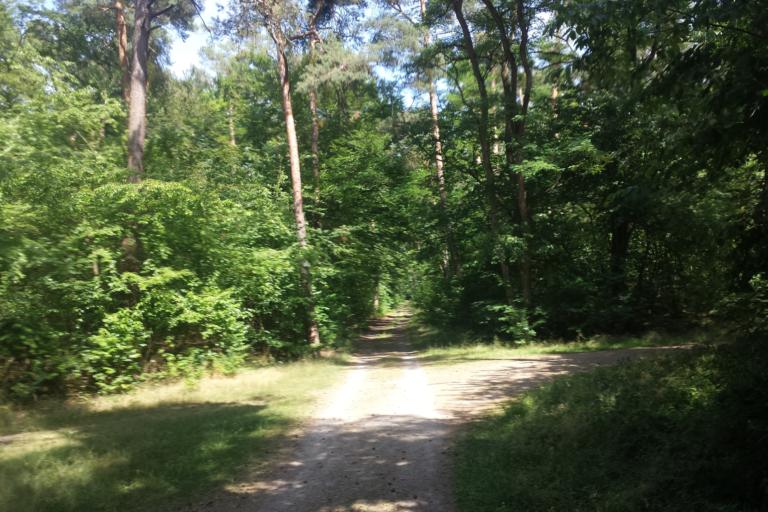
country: DE
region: Hesse
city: Lampertheim
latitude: 49.5611
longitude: 8.5030
